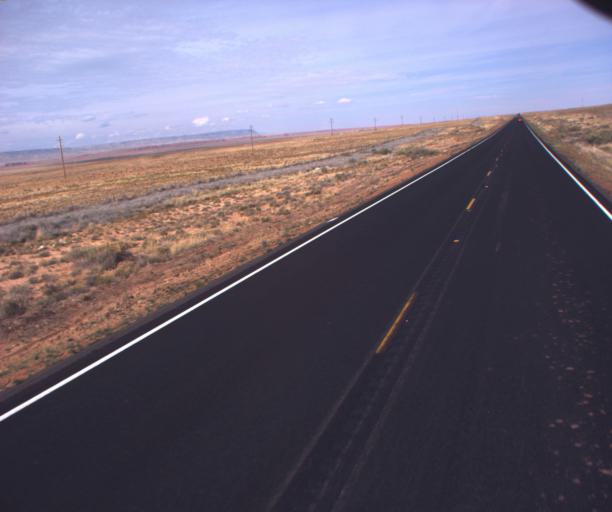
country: US
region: Arizona
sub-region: Apache County
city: Chinle
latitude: 36.0306
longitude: -109.6064
